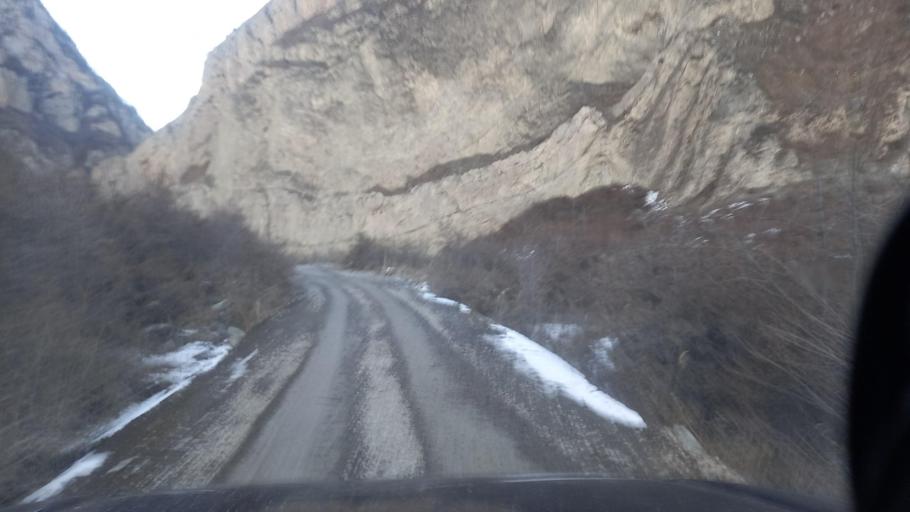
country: RU
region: Ingushetiya
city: Dzhayrakh
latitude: 42.8610
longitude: 44.5198
